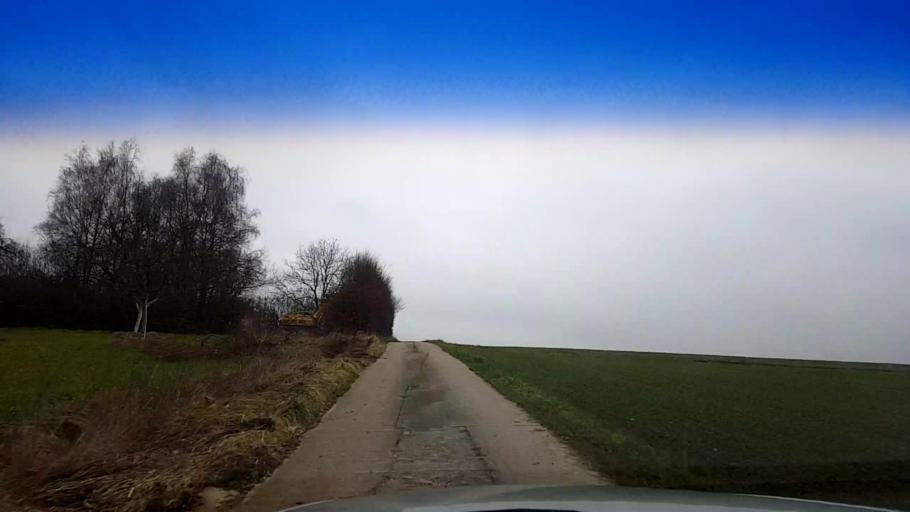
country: DE
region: Bavaria
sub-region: Upper Franconia
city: Memmelsdorf
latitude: 49.9734
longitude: 10.9790
